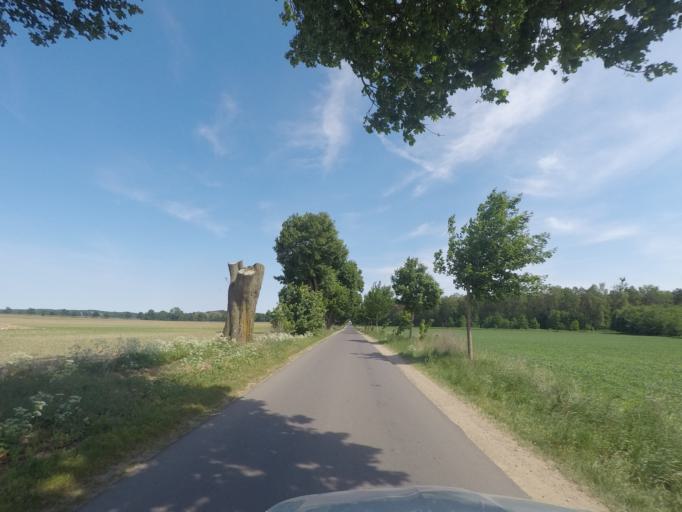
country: DE
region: Brandenburg
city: Britz
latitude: 52.8905
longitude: 13.7947
